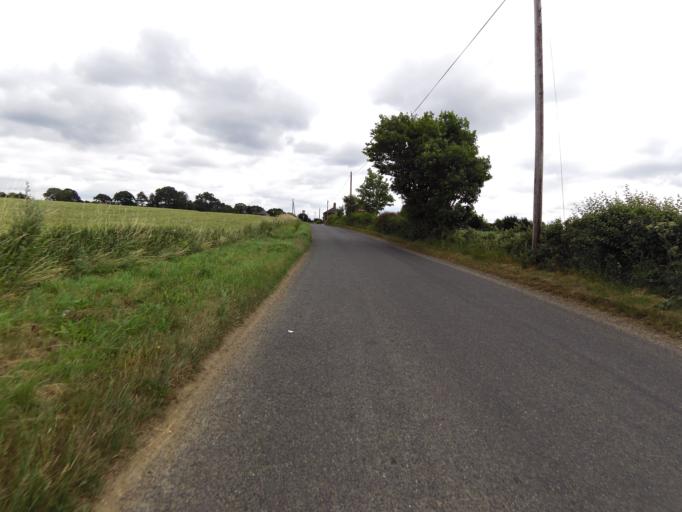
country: GB
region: England
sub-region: Norfolk
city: Harleston
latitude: 52.4015
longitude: 1.2689
